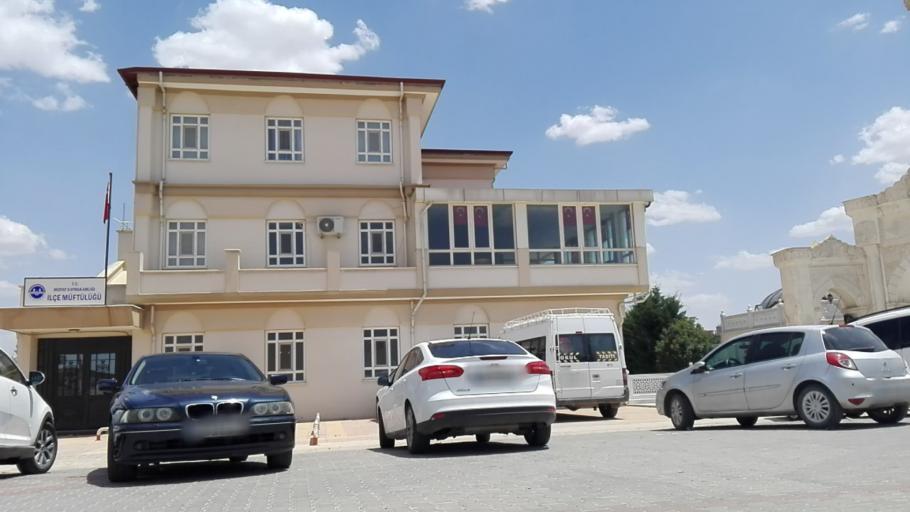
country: TR
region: Mardin
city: Midyat
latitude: 37.4196
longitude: 41.3614
